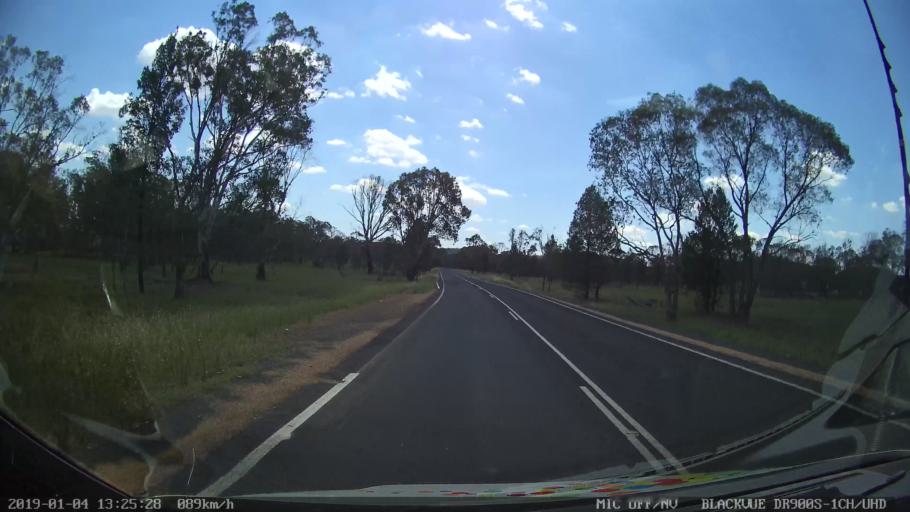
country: AU
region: New South Wales
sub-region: Parkes
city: Peak Hill
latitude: -32.6925
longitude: 148.5556
